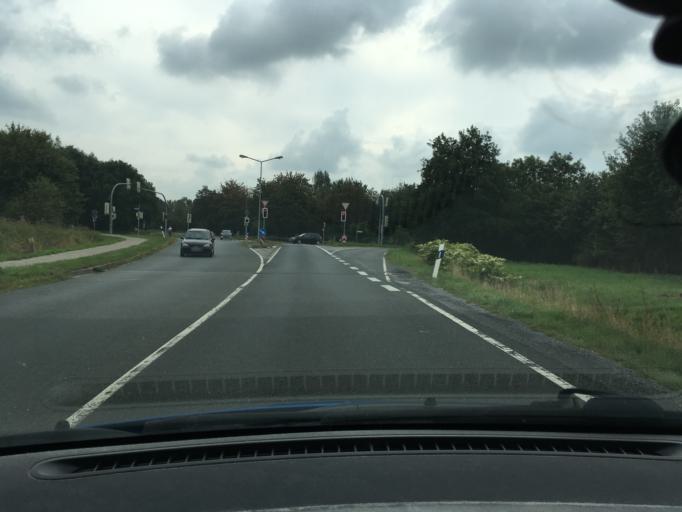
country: DE
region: Lower Saxony
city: Garbsen
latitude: 52.4325
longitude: 9.5750
